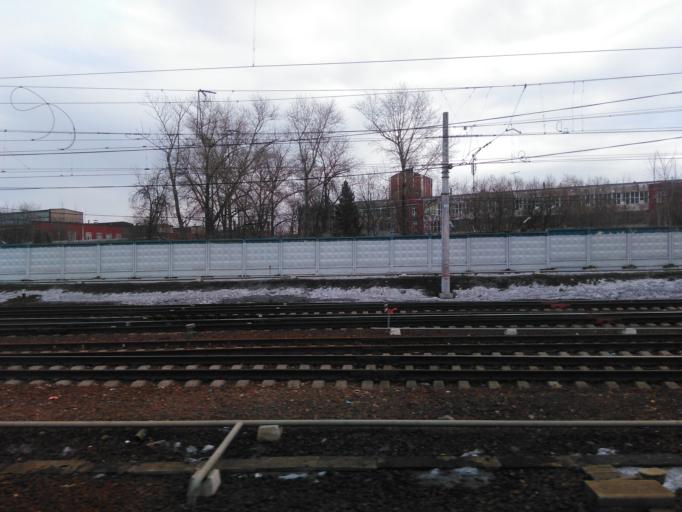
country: RU
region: Moskovskaya
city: Mytishchi
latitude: 55.9131
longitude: 37.7595
